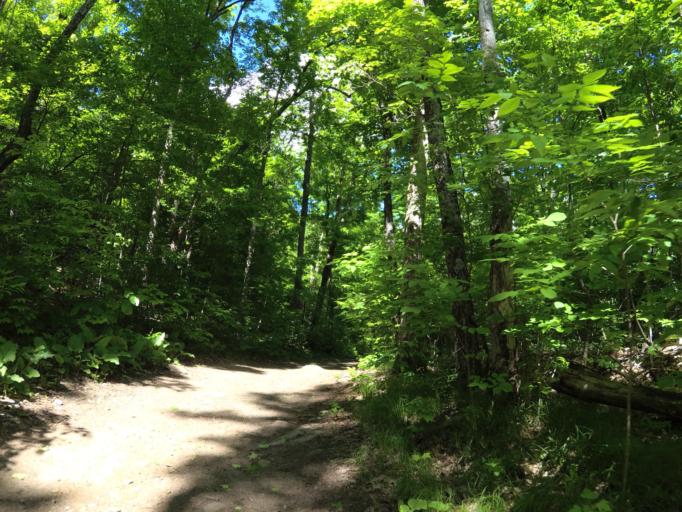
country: CA
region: Ontario
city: Renfrew
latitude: 45.0441
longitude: -76.8399
